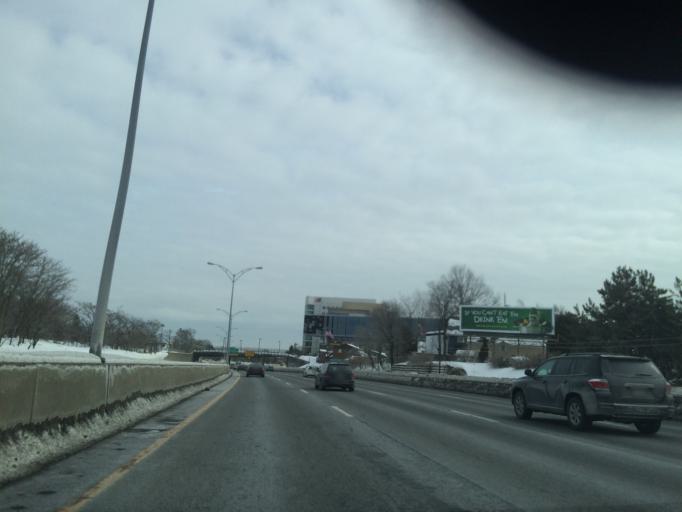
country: US
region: Massachusetts
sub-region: Middlesex County
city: Watertown
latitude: 42.3579
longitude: -71.1516
